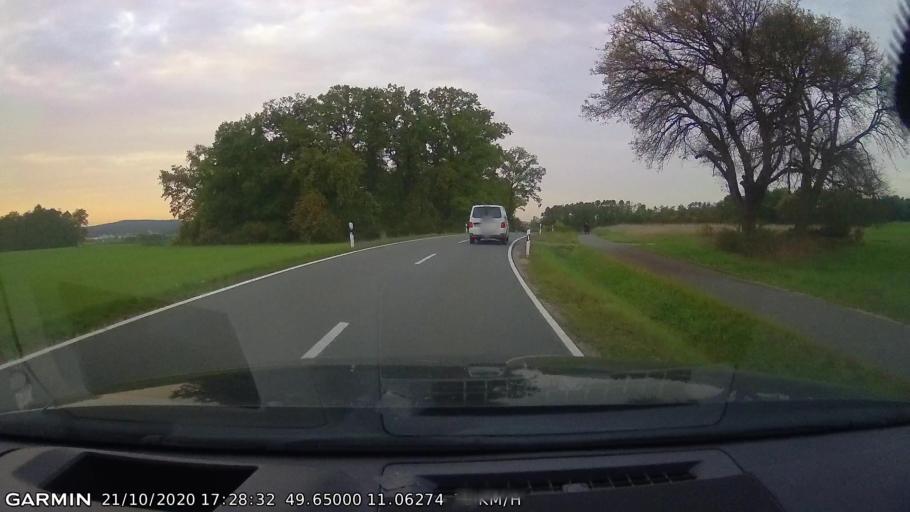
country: DE
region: Bavaria
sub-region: Upper Franconia
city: Langensendelbach
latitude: 49.6500
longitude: 11.0629
